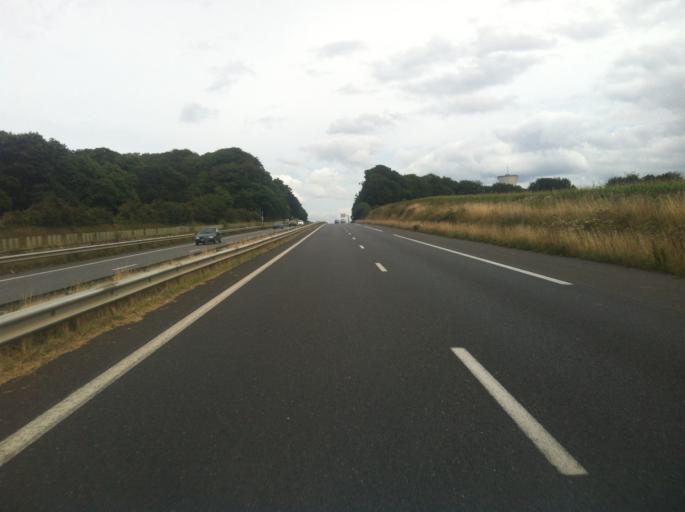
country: FR
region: Brittany
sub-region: Departement du Finistere
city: Morlaix
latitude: 48.5631
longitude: -3.8633
